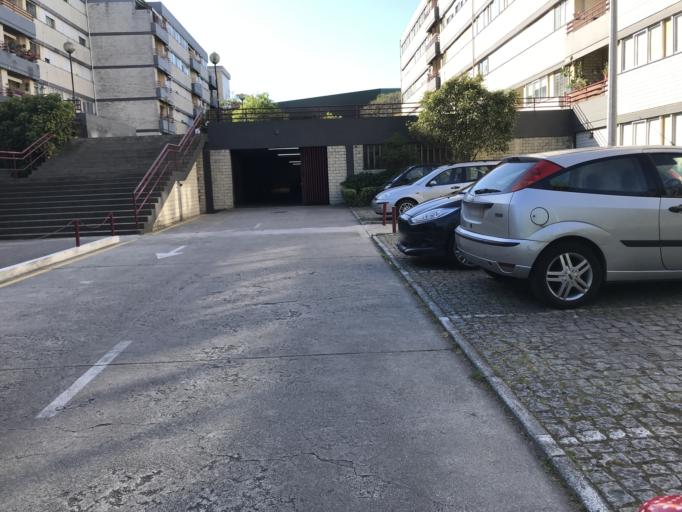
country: PT
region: Porto
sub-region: Matosinhos
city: Matosinhos
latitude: 41.1815
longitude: -8.6775
